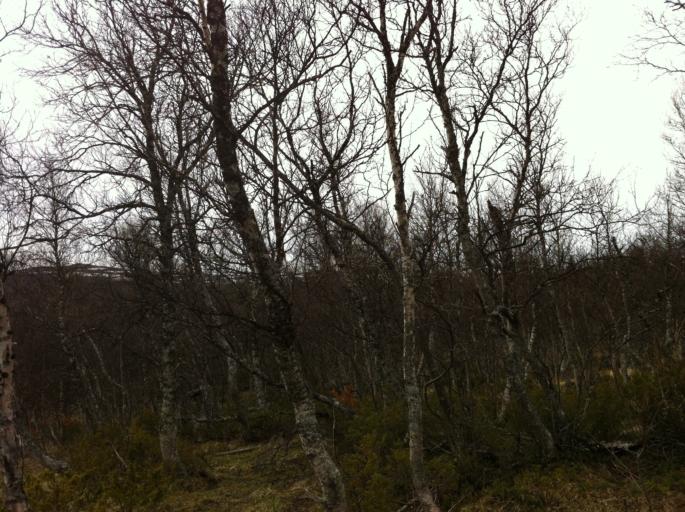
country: NO
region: Sor-Trondelag
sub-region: Tydal
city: Aas
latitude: 62.5557
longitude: 12.3130
